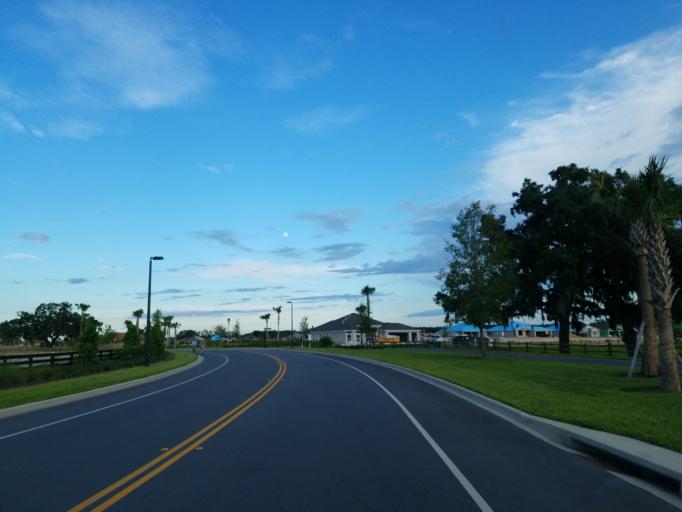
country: US
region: Florida
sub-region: Sumter County
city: Wildwood
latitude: 28.7905
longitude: -82.0188
